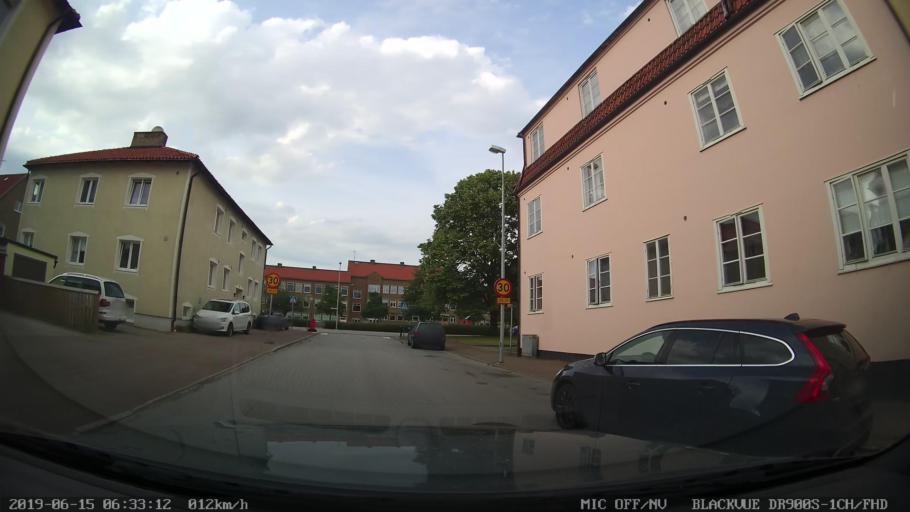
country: SE
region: Skane
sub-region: Landskrona
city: Landskrona
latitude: 55.8749
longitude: 12.8452
